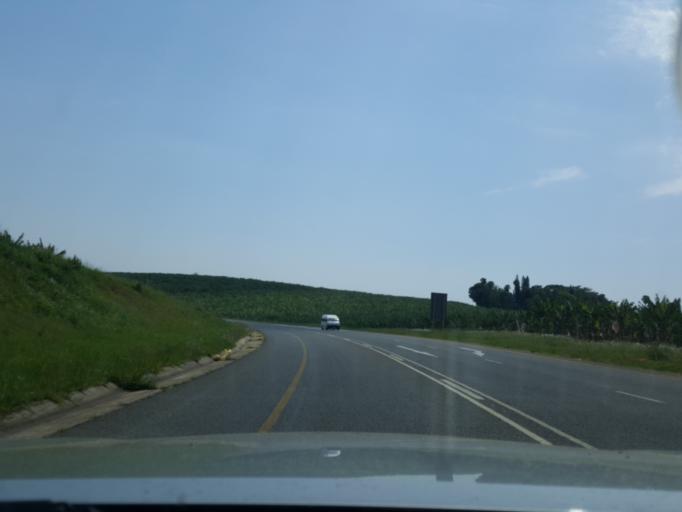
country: ZA
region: Mpumalanga
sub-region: Ehlanzeni District
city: White River
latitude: -25.0802
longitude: 31.1017
